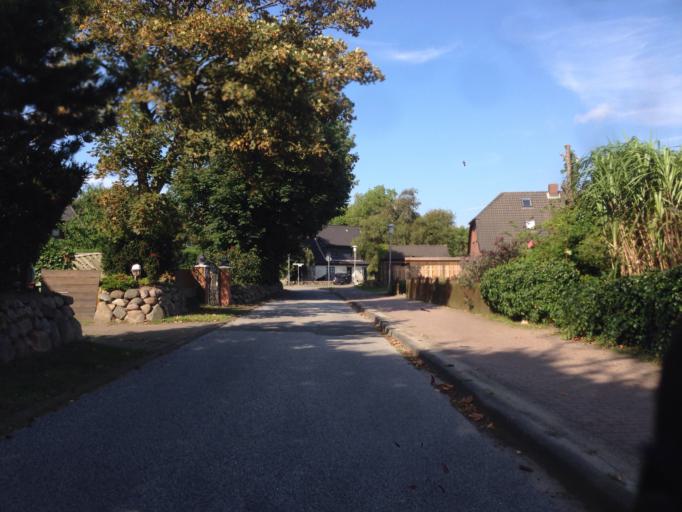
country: DE
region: Schleswig-Holstein
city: Westerland
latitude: 54.9084
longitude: 8.3191
